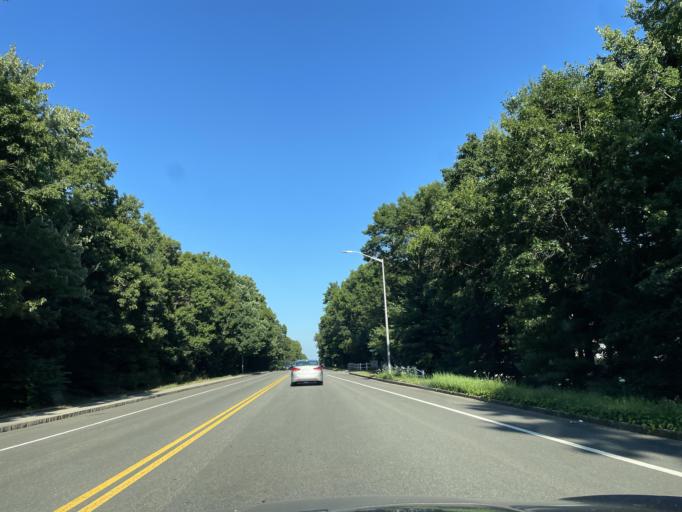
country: US
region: Massachusetts
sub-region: Bristol County
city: Easton
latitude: 42.0274
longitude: -71.1715
